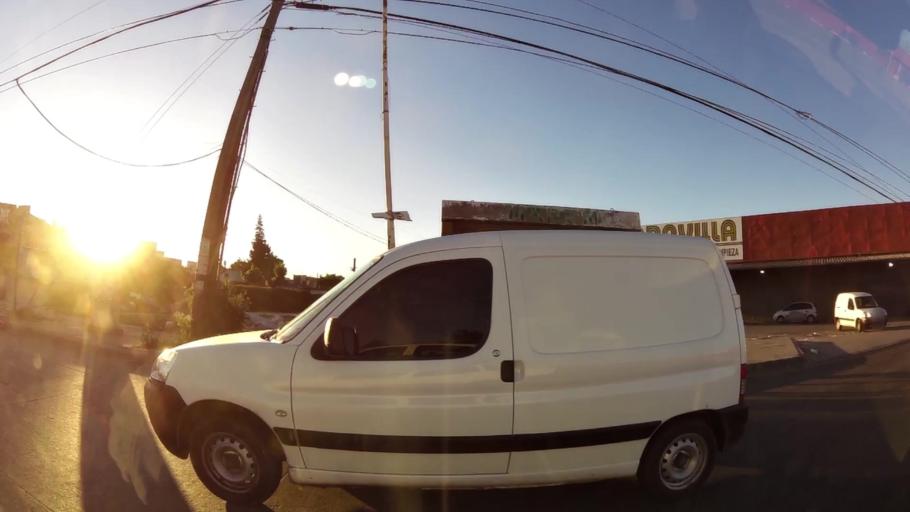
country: AR
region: Buenos Aires
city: San Justo
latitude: -34.7390
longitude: -58.6052
